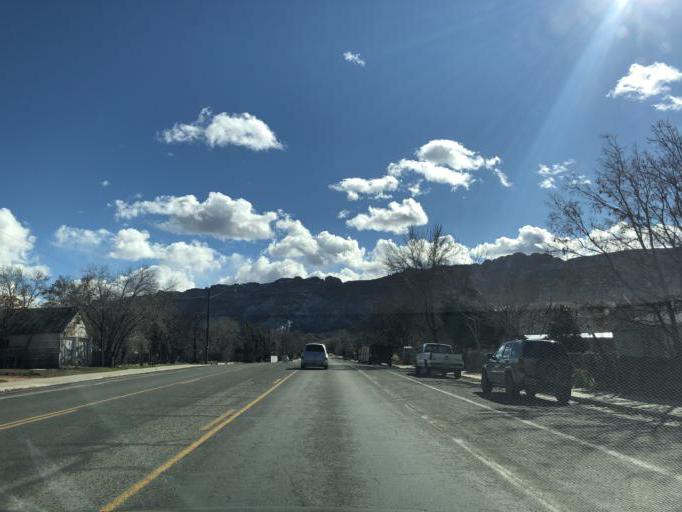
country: US
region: Utah
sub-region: Grand County
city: Moab
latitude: 38.5730
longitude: -109.5430
